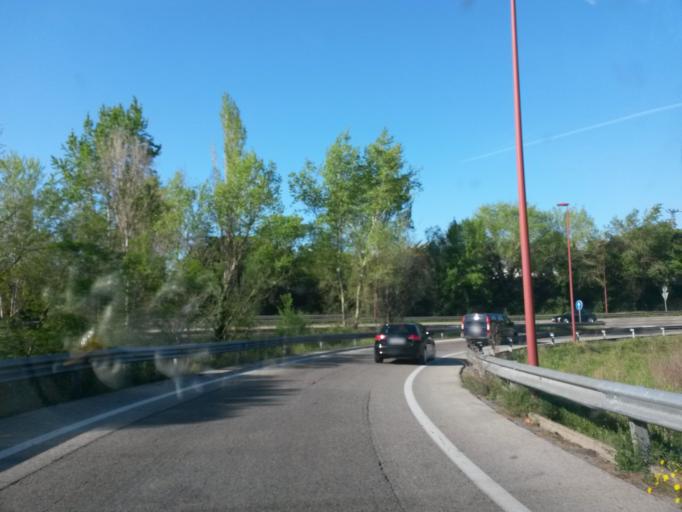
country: ES
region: Catalonia
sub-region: Provincia de Girona
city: Sarria de Ter
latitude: 42.0319
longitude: 2.8280
